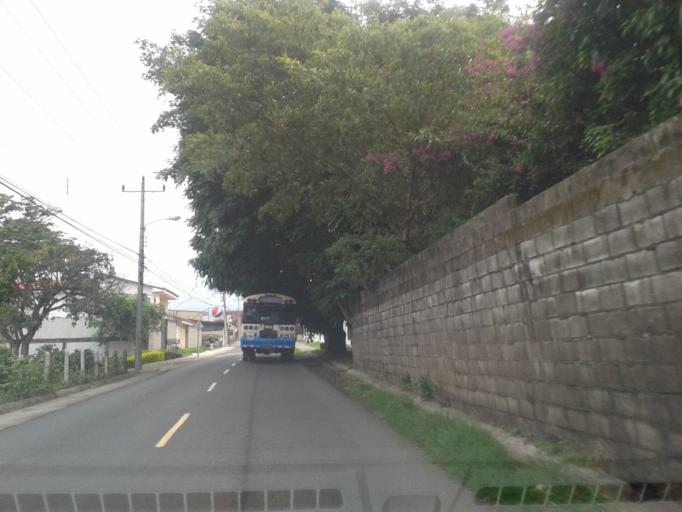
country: CR
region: Heredia
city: Mercedes
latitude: 9.9991
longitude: -84.1378
